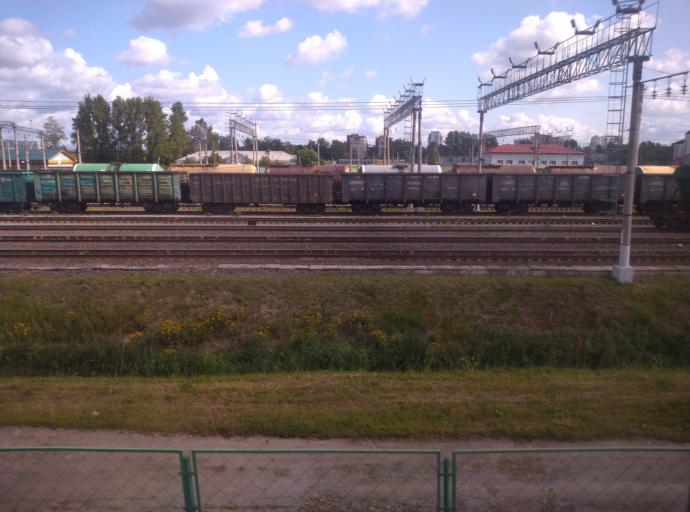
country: RU
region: St.-Petersburg
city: Obukhovo
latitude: 59.8646
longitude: 30.4290
